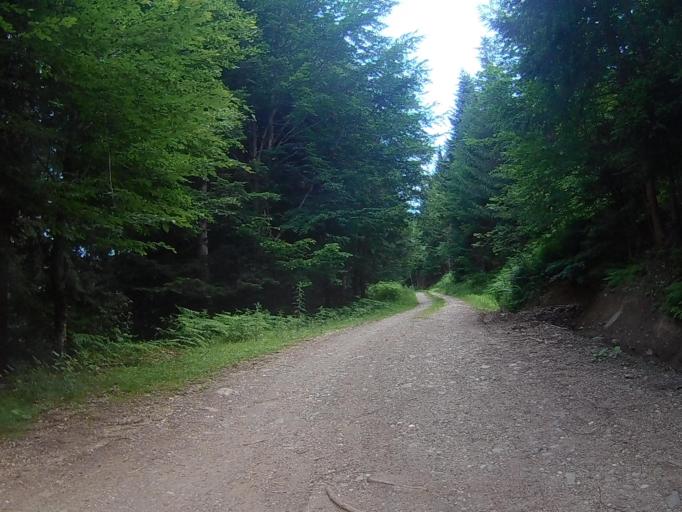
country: SI
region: Selnica ob Dravi
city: Selnica ob Dravi
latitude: 46.5131
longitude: 15.4750
